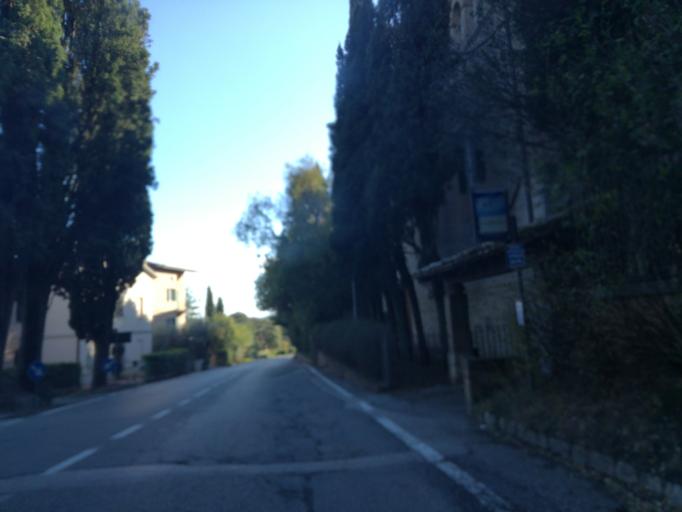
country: IT
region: Umbria
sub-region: Provincia di Perugia
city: Perugia
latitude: 43.0843
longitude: 12.4001
